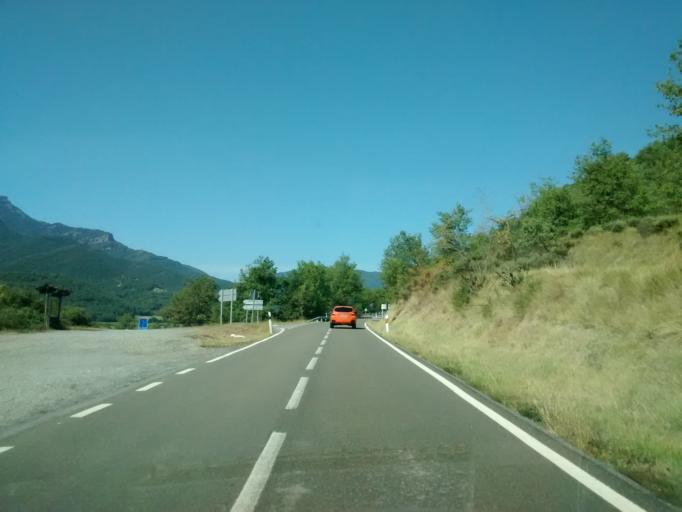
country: ES
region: Aragon
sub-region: Provincia de Huesca
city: Fiscal
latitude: 42.4798
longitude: -0.0758
